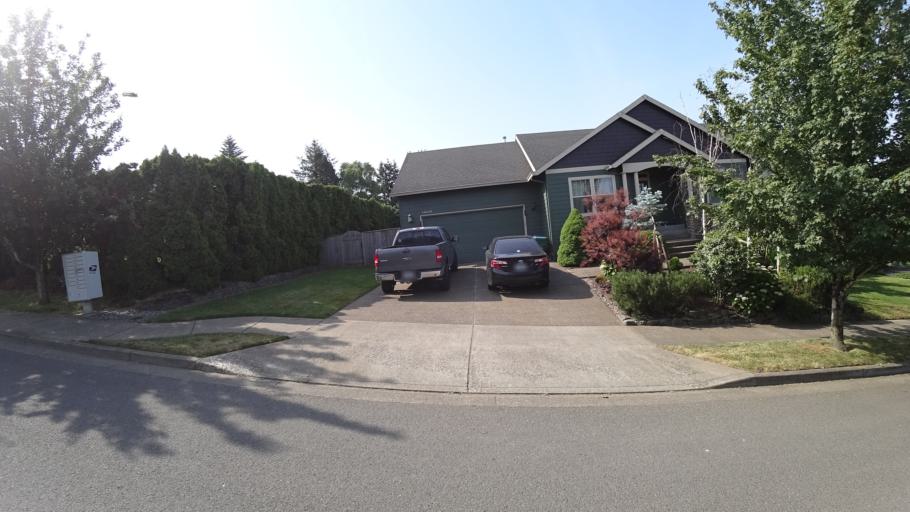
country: US
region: Oregon
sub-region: Clackamas County
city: Happy Valley
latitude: 45.4600
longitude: -122.5228
